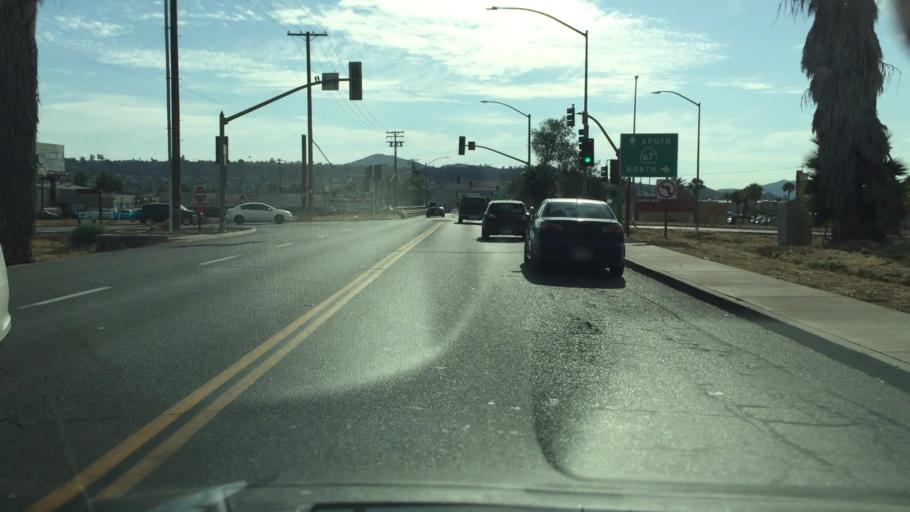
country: US
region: California
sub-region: San Diego County
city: Santee
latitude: 32.8192
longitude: -116.9593
